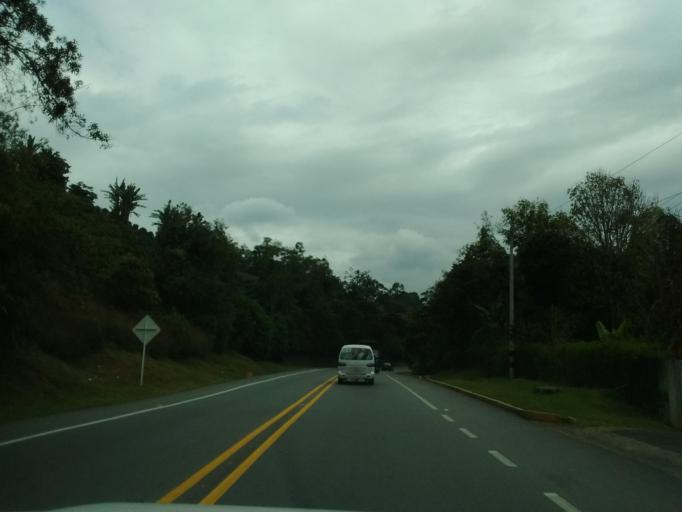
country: CO
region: Cauca
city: Cajibio
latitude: 2.6097
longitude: -76.5276
